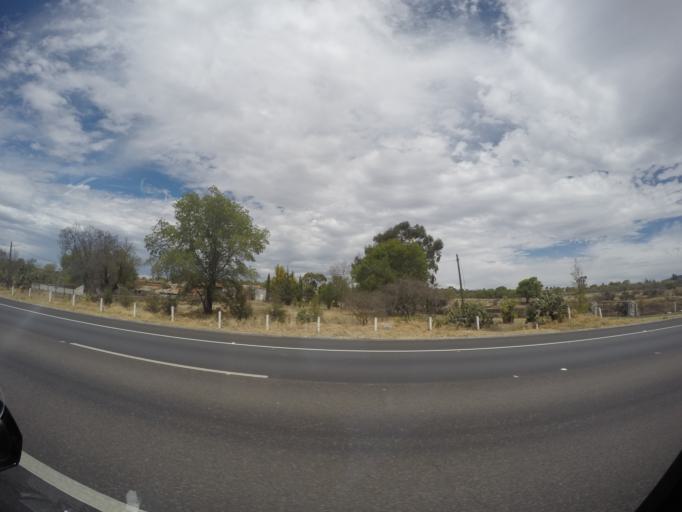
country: MX
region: Mexico
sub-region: Aculco
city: El Colorado
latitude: 20.1540
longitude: -99.7422
